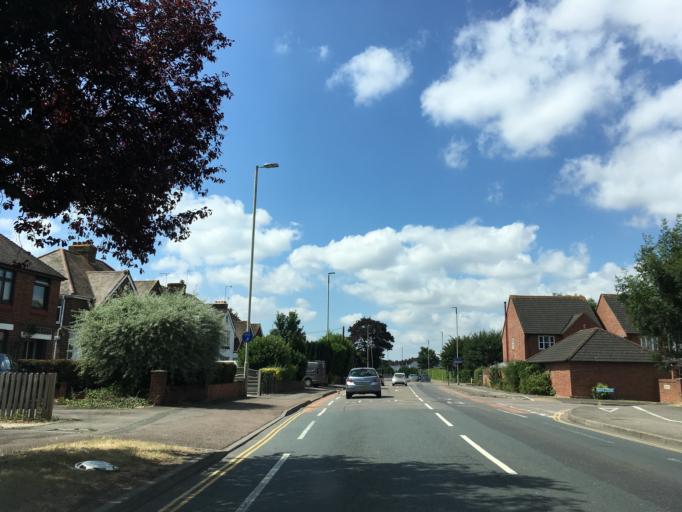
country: GB
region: England
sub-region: Gloucestershire
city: Barnwood
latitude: 51.8777
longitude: -2.2024
